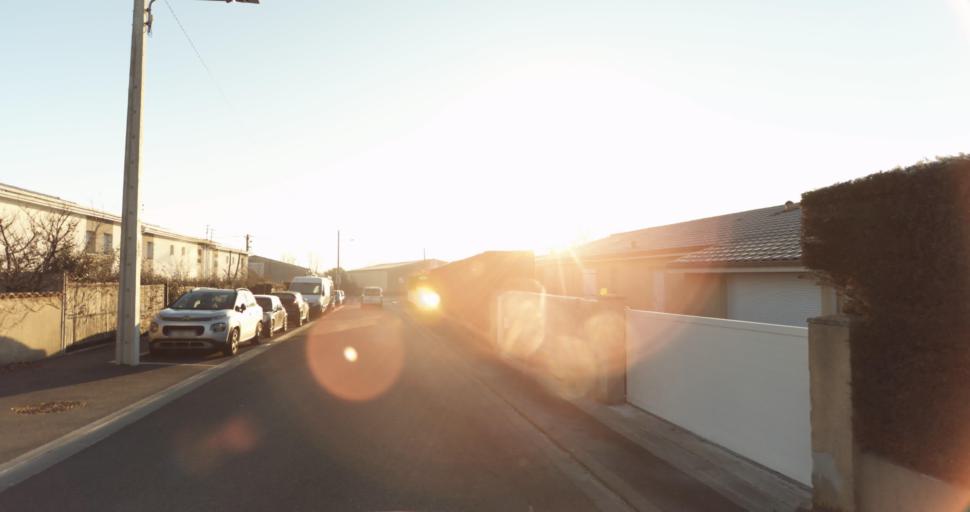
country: FR
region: Aquitaine
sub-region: Departement de la Gironde
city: Ambares-et-Lagrave
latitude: 44.9149
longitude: -0.4943
